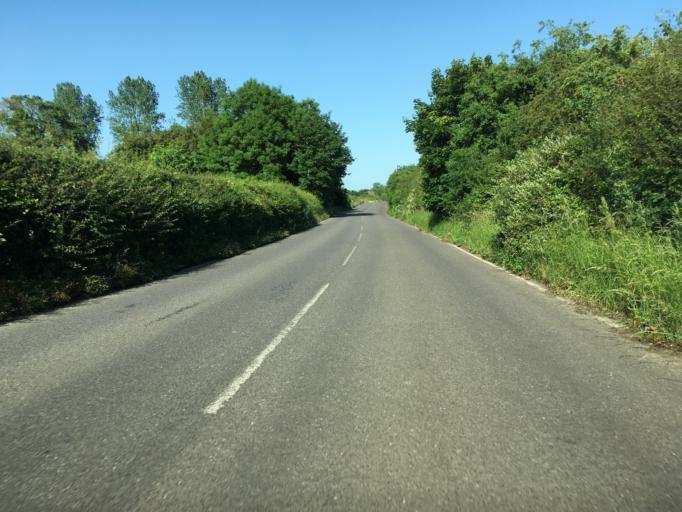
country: GB
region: England
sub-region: Oxfordshire
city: Bicester
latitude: 51.9238
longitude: -1.1344
